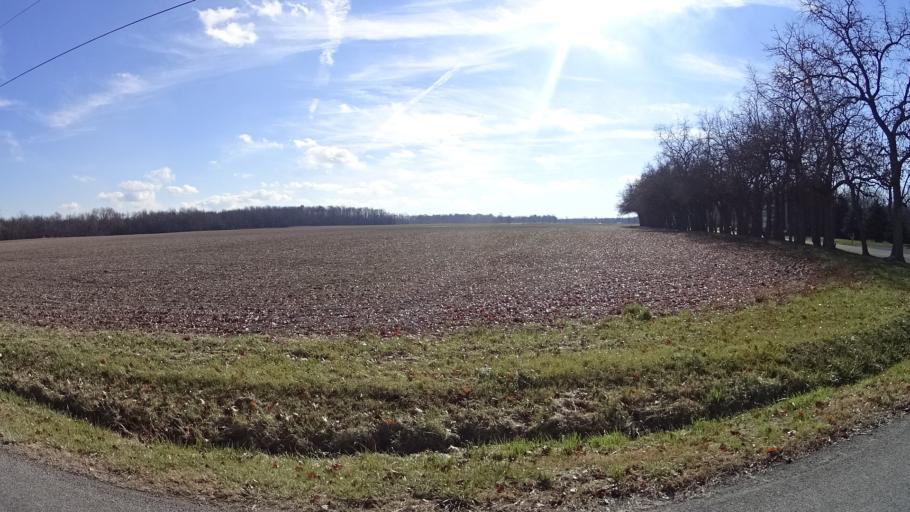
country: US
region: Ohio
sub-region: Lorain County
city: Wellington
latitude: 41.0860
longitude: -82.1695
